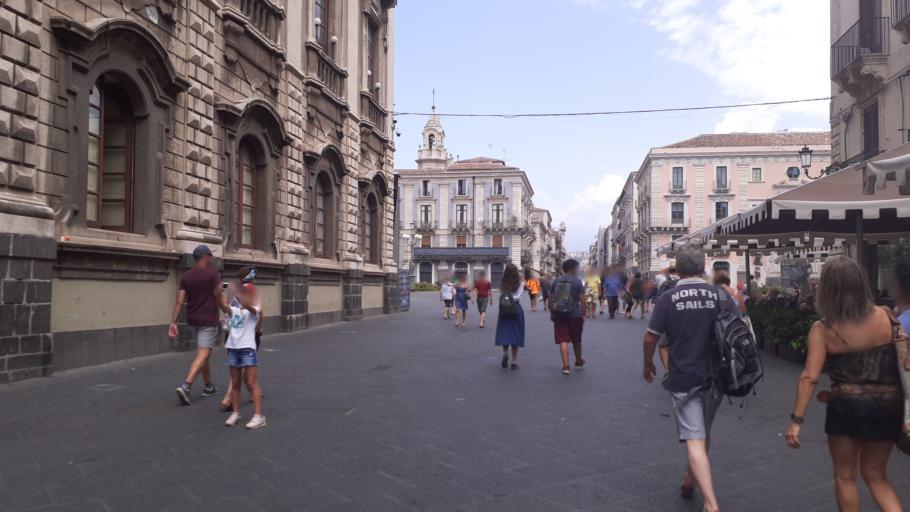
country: IT
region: Sicily
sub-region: Catania
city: Catania
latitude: 37.5030
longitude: 15.0874
